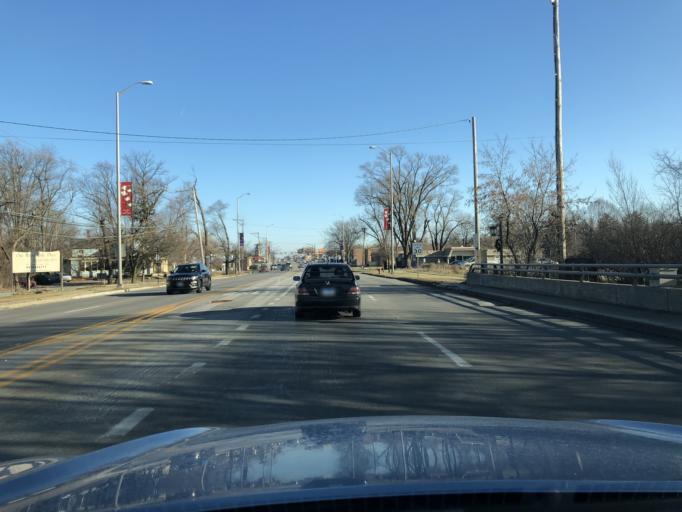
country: US
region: Illinois
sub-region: DuPage County
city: Wood Dale
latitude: 41.9643
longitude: -87.9844
